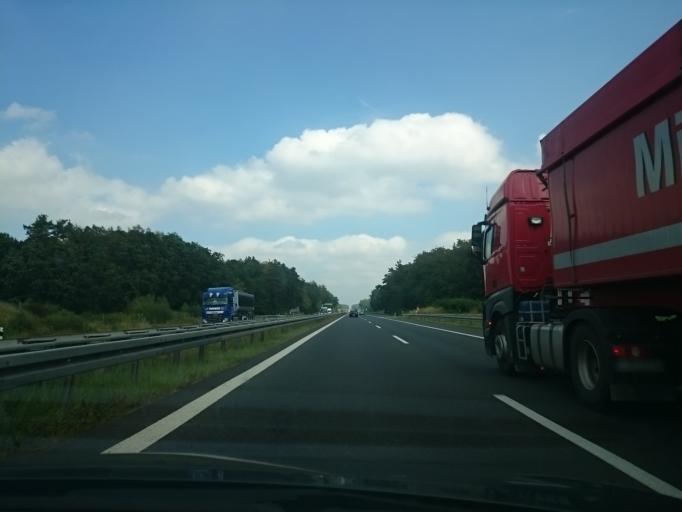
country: DE
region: Brandenburg
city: Joachimsthal
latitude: 52.8901
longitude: 13.7152
